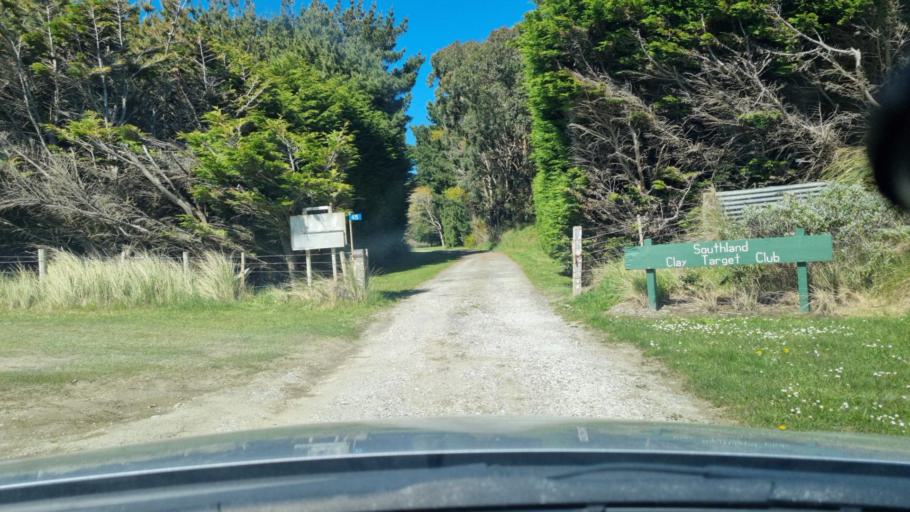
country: NZ
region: Southland
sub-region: Invercargill City
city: Invercargill
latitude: -46.4408
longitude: 168.2400
